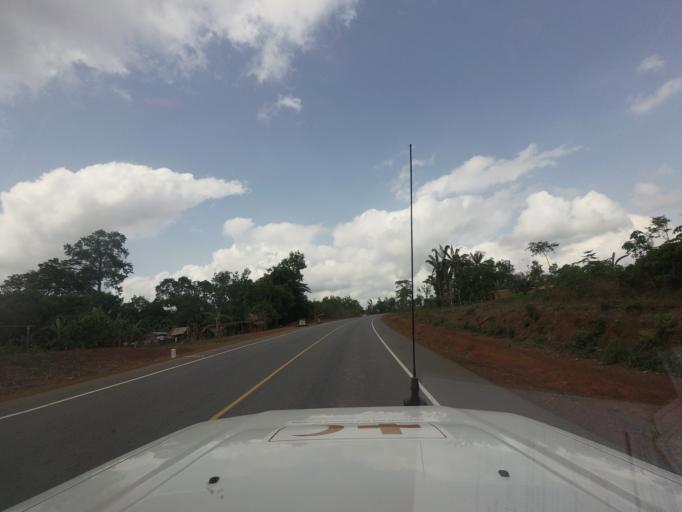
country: LR
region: Nimba
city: Sanniquellie
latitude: 7.1642
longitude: -9.0407
